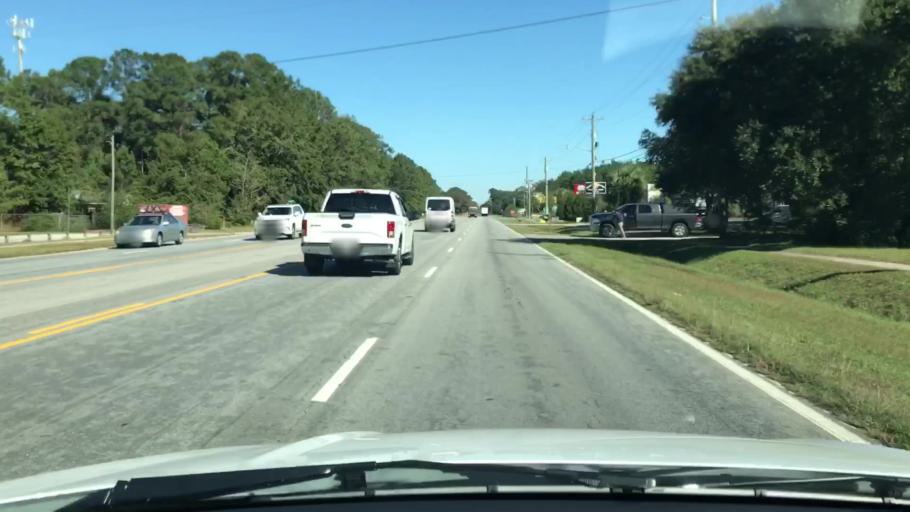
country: US
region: South Carolina
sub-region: Charleston County
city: Ravenel
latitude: 32.7771
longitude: -80.2434
